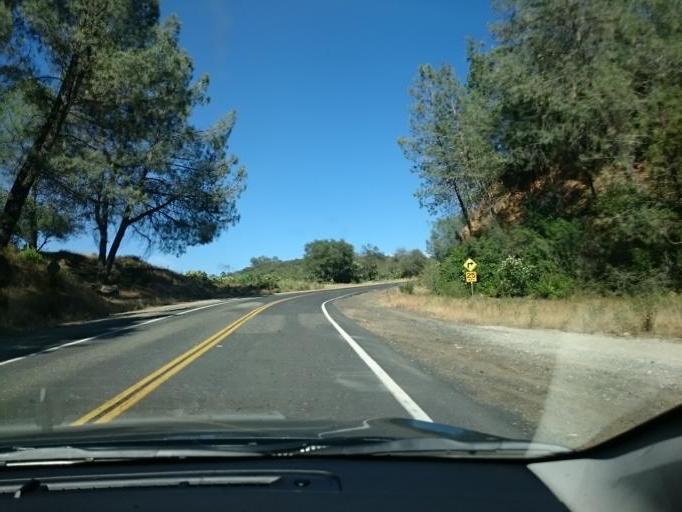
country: US
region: California
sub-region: Tuolumne County
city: Columbia
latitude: 38.0534
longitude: -120.4326
